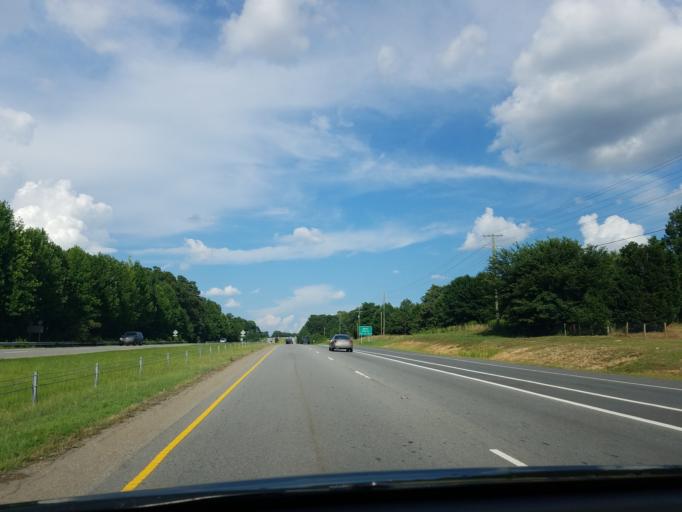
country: US
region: North Carolina
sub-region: Wake County
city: Apex
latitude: 35.7491
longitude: -78.8641
